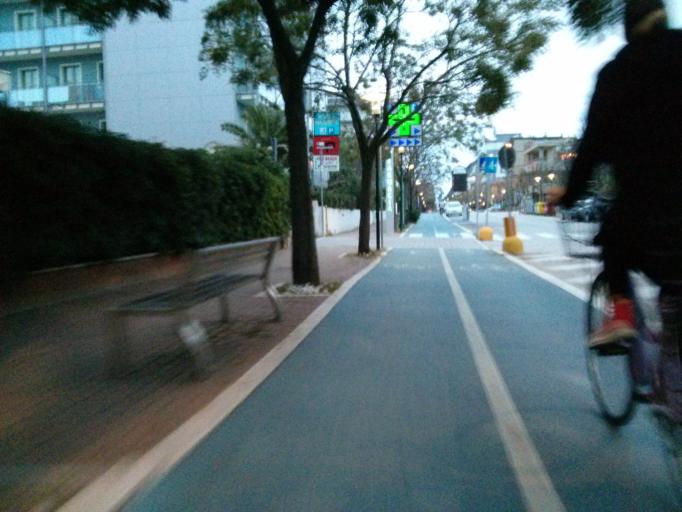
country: IT
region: The Marches
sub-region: Provincia di Pesaro e Urbino
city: Pesaro
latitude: 43.9100
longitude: 12.9232
